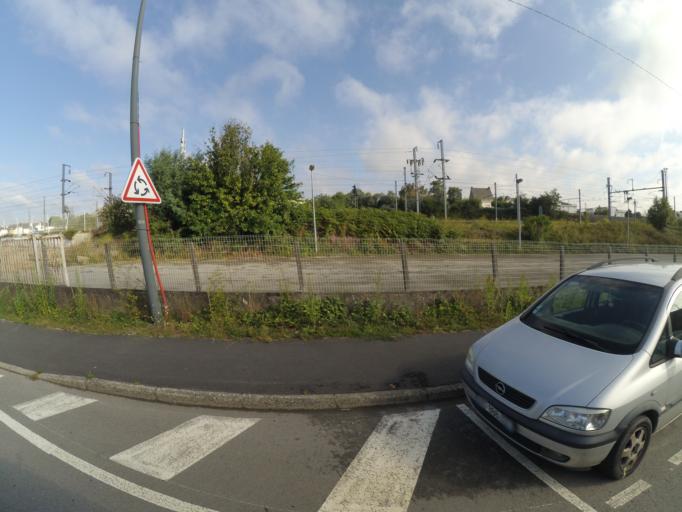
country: FR
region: Brittany
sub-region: Departement du Morbihan
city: Vannes
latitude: 47.6664
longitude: -2.7480
